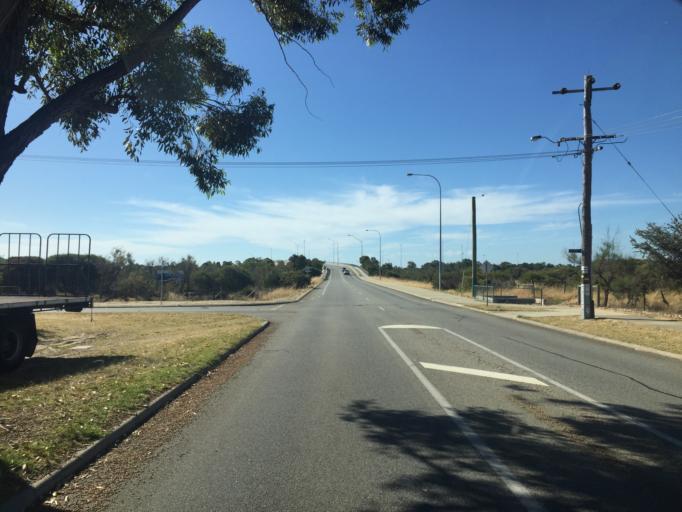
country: AU
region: Western Australia
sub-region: Gosnells
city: Kenwick
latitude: -32.0301
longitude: 115.9748
